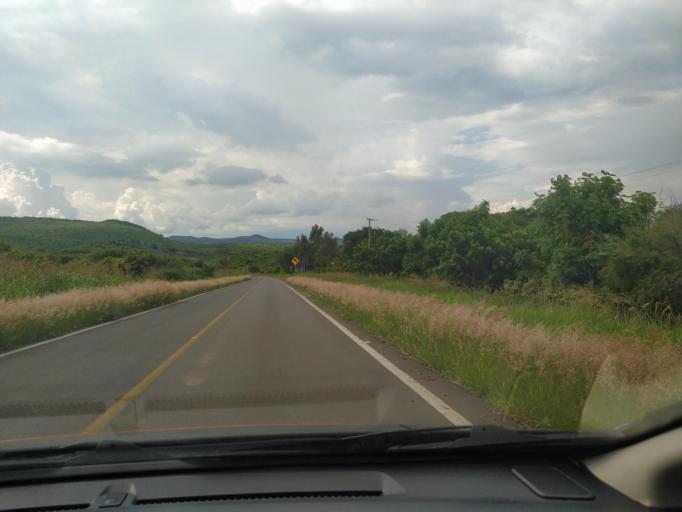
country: MX
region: Jalisco
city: Villa Corona
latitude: 20.3987
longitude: -103.6797
